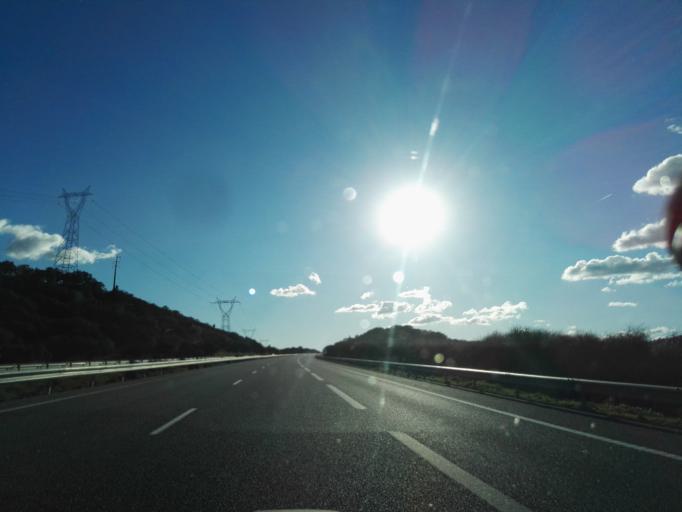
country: PT
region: Evora
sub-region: Estremoz
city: Estremoz
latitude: 38.7747
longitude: -7.6919
